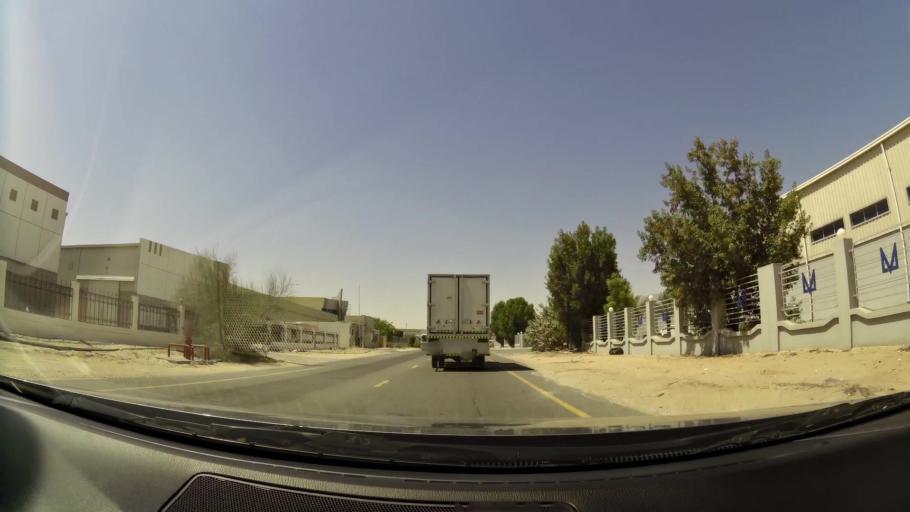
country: AE
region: Dubai
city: Dubai
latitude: 24.9866
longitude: 55.2071
